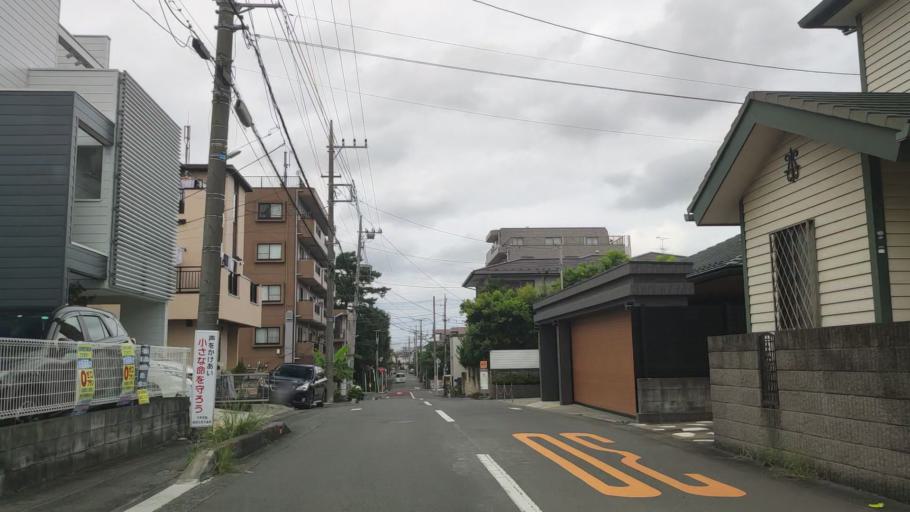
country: JP
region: Kanagawa
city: Minami-rinkan
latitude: 35.5077
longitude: 139.4401
